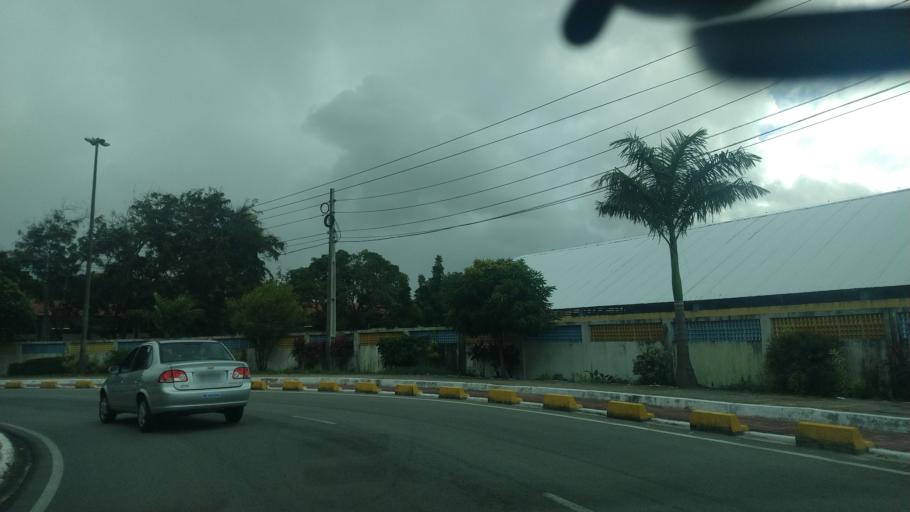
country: BR
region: Rio Grande do Norte
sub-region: Natal
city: Natal
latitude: -5.8374
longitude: -35.2054
